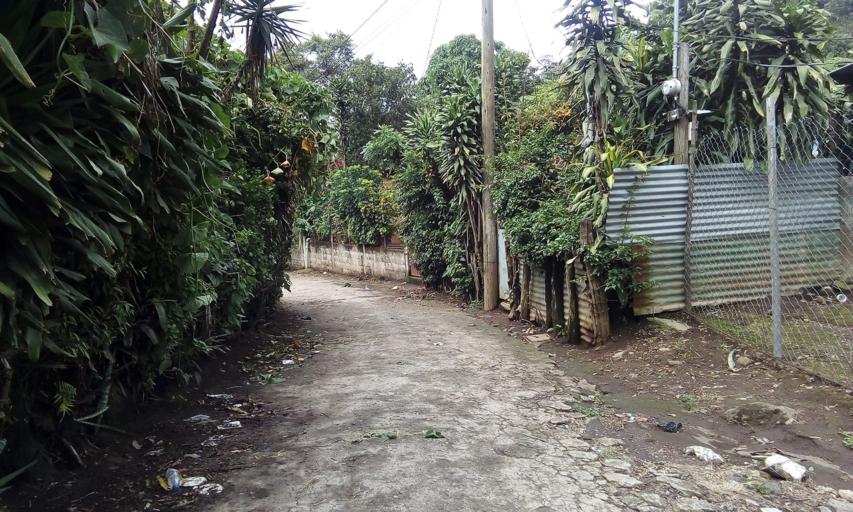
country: GT
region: Escuintla
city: San Vicente Pacaya
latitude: 14.3317
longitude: -90.6025
